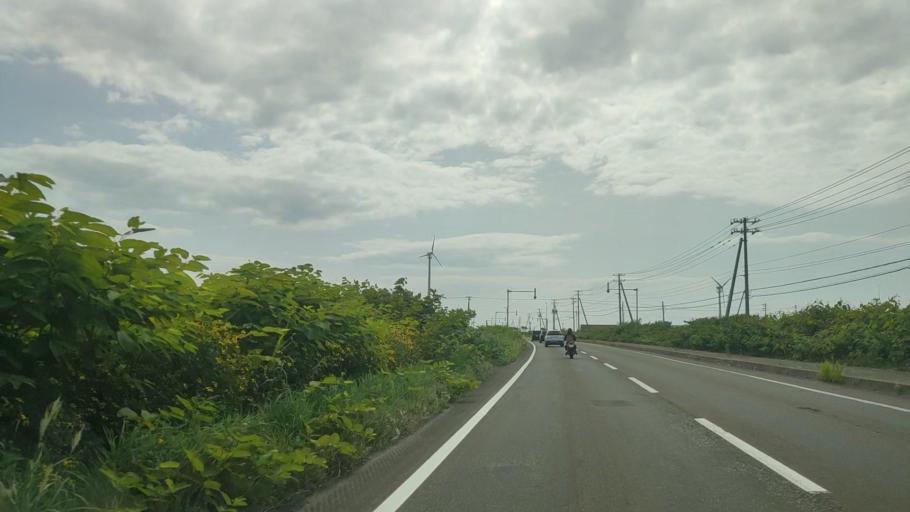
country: JP
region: Hokkaido
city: Rumoi
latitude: 44.3971
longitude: 141.7202
